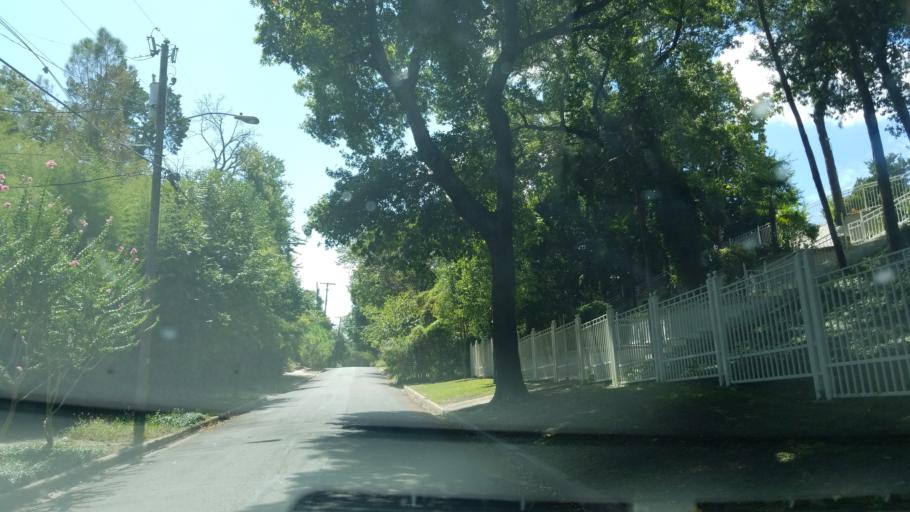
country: US
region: Texas
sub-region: Dallas County
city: Dallas
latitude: 32.7613
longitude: -96.8298
